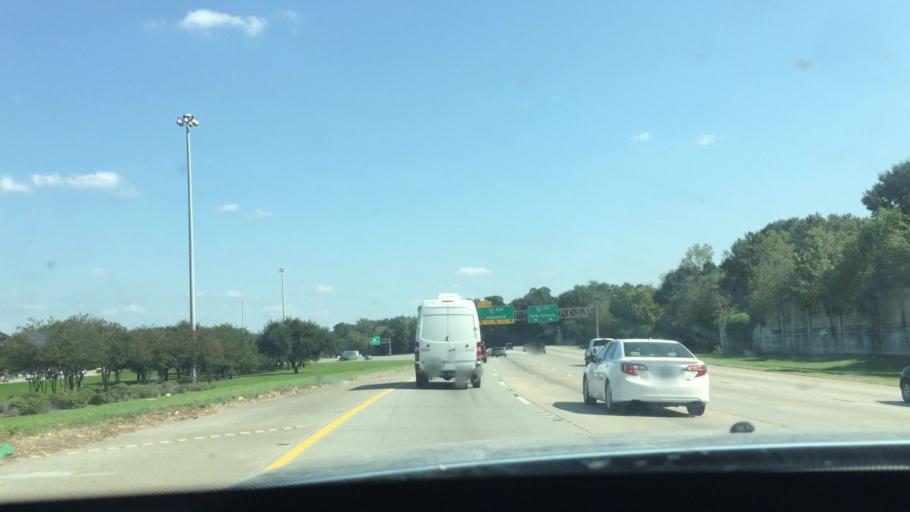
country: US
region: Louisiana
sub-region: East Baton Rouge Parish
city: Westminster
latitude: 30.4202
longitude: -91.1220
